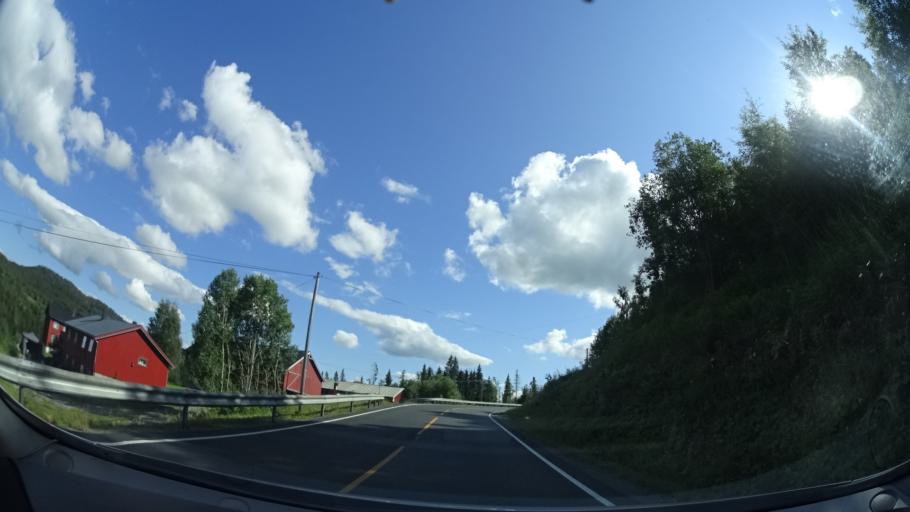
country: NO
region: Sor-Trondelag
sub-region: Snillfjord
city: Krokstadora
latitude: 63.2382
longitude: 9.5924
